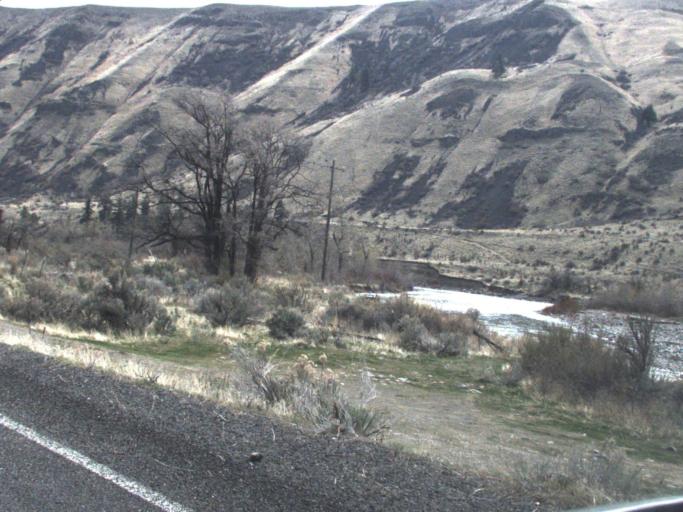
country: US
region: Washington
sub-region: Yakima County
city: Tieton
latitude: 46.7522
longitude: -120.8174
